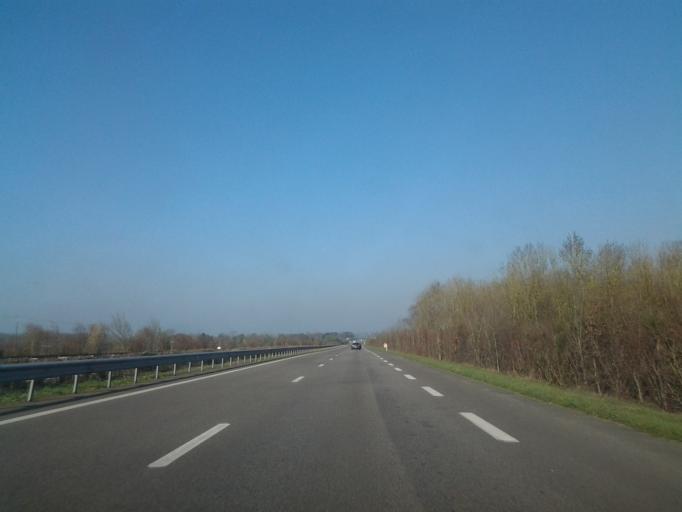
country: FR
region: Pays de la Loire
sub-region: Departement de la Vendee
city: Mache
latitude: 46.7958
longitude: -1.7167
